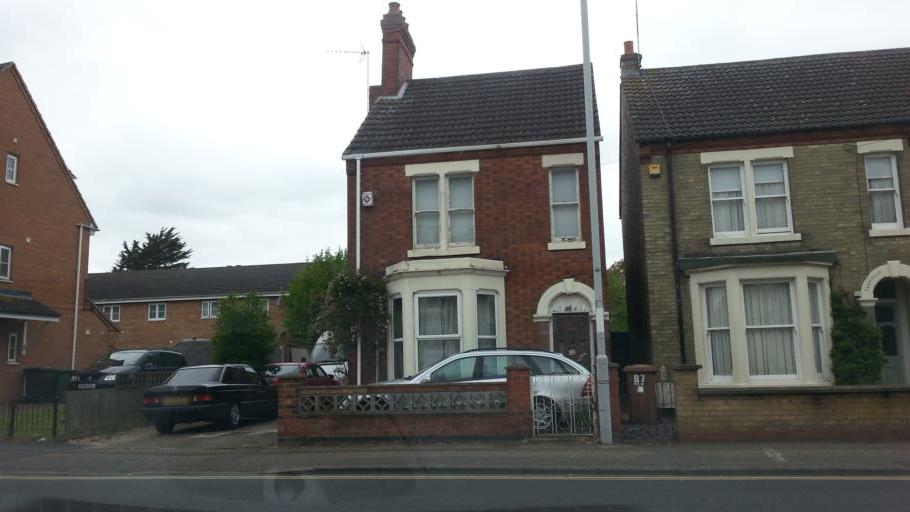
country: GB
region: England
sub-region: Peterborough
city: Peterborough
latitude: 52.5848
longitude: -0.2427
